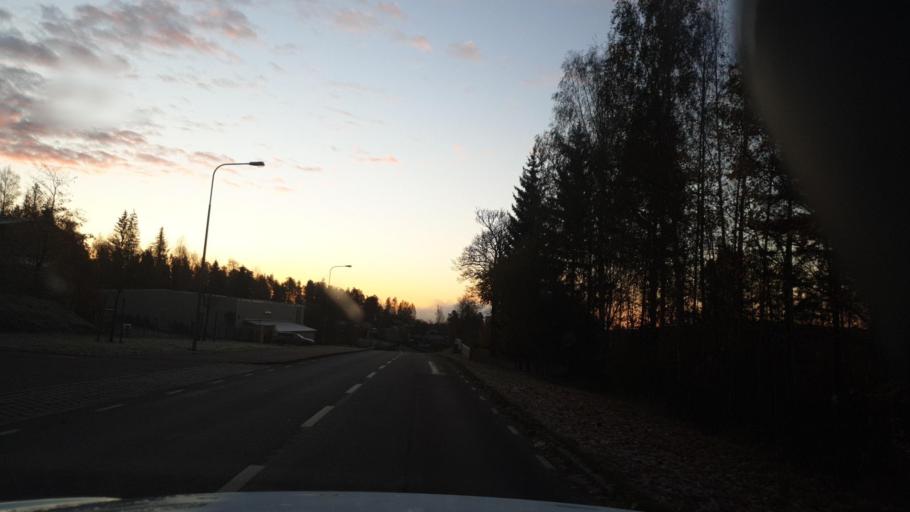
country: SE
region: Vaermland
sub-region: Eda Kommun
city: Amotfors
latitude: 59.7682
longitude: 12.3539
